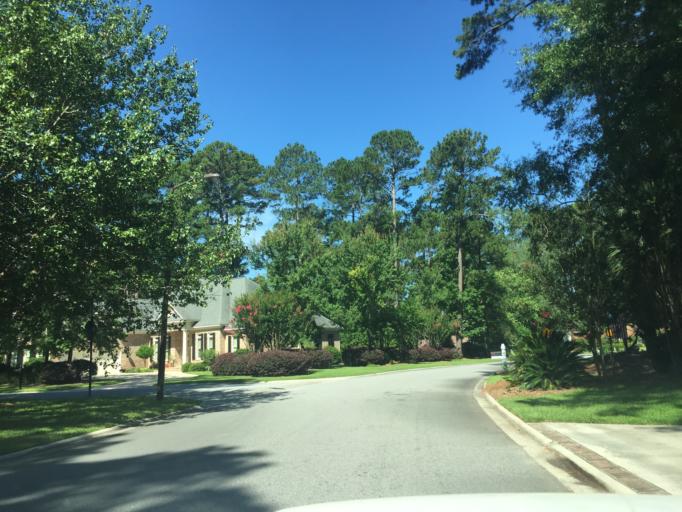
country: US
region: Georgia
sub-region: Chatham County
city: Pooler
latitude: 32.0656
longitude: -81.2202
